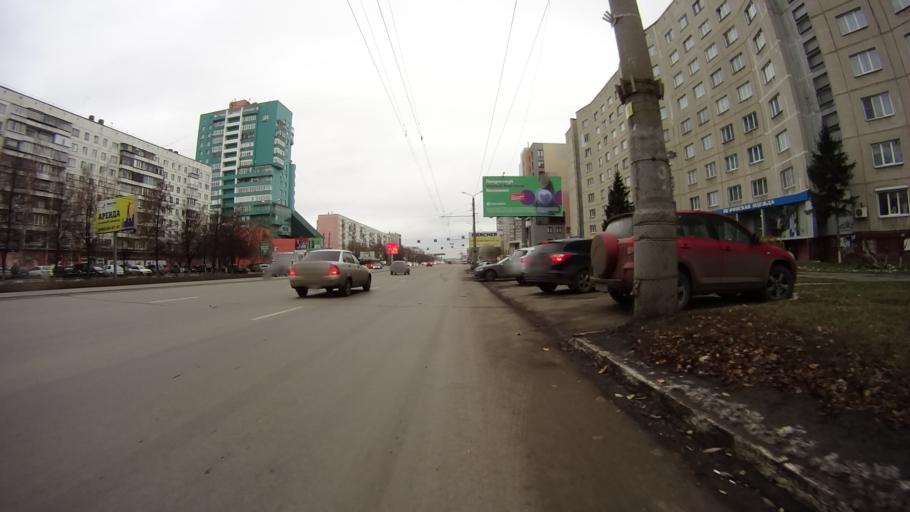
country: RU
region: Chelyabinsk
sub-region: Gorod Chelyabinsk
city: Chelyabinsk
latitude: 55.1942
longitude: 61.3289
